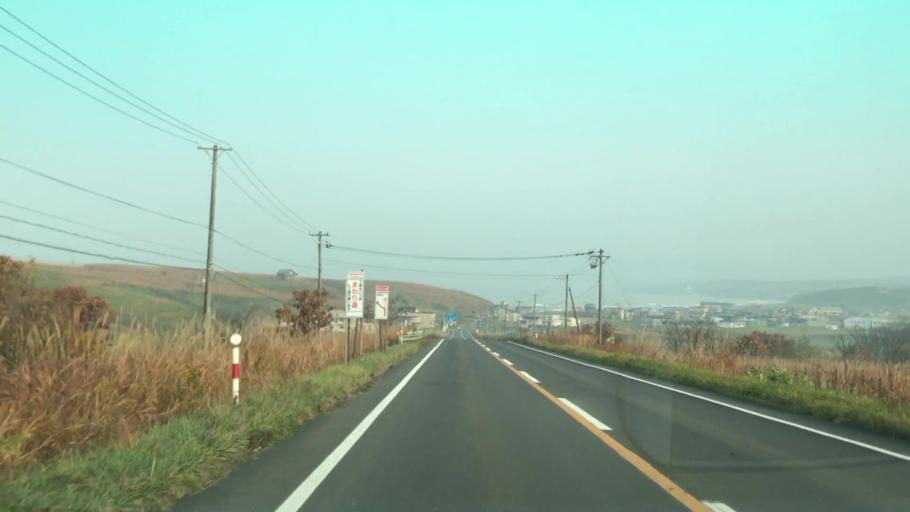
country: JP
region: Hokkaido
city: Ishikari
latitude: 43.3079
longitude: 141.4123
